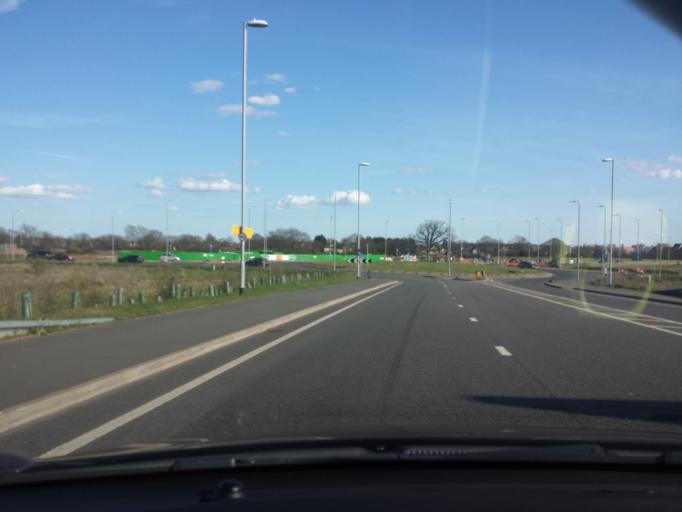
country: GB
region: England
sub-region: Essex
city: Great Horkesley
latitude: 51.9236
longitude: 0.9021
